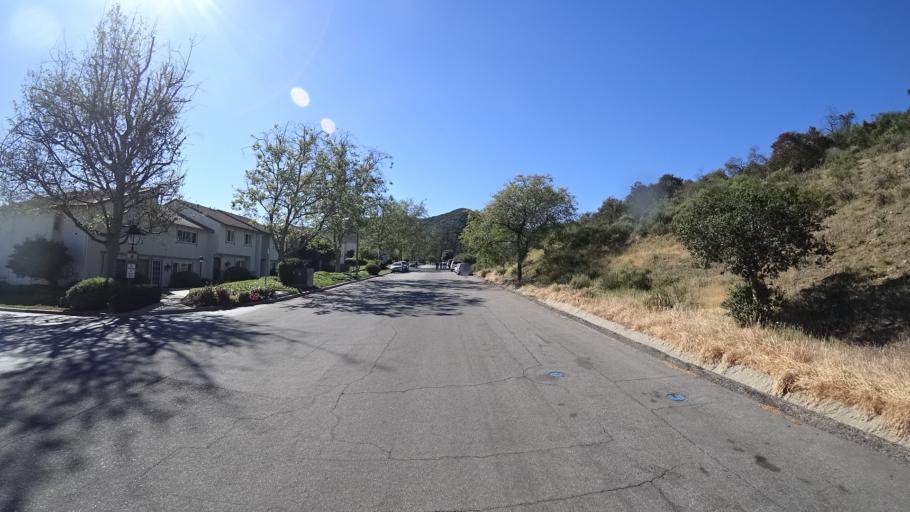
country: US
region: California
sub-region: Ventura County
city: Thousand Oaks
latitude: 34.1738
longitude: -118.8817
